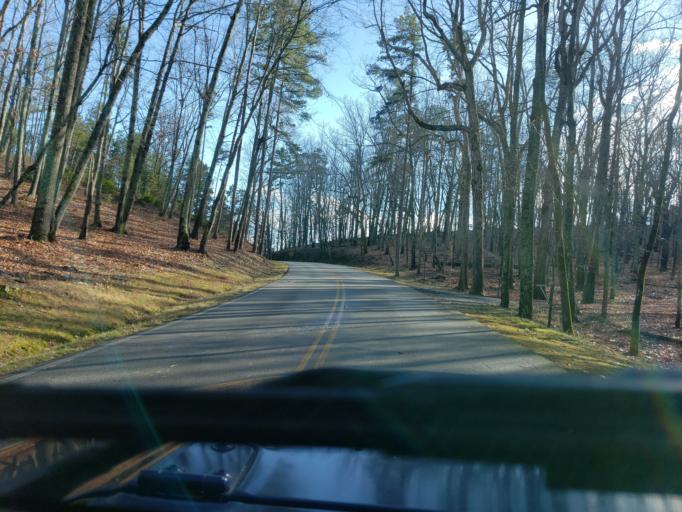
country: US
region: North Carolina
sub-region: Cleveland County
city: White Plains
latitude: 35.1400
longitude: -81.3868
